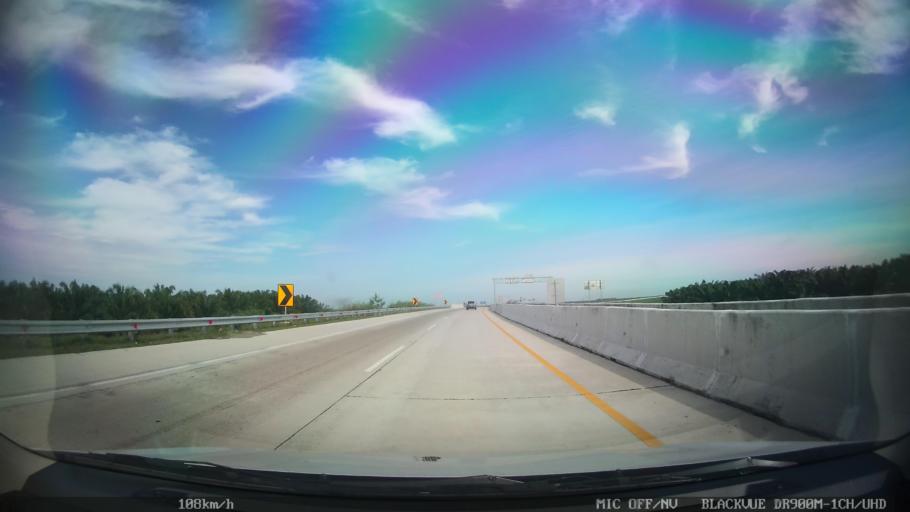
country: ID
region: North Sumatra
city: Binjai
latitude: 3.6522
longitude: 98.5371
